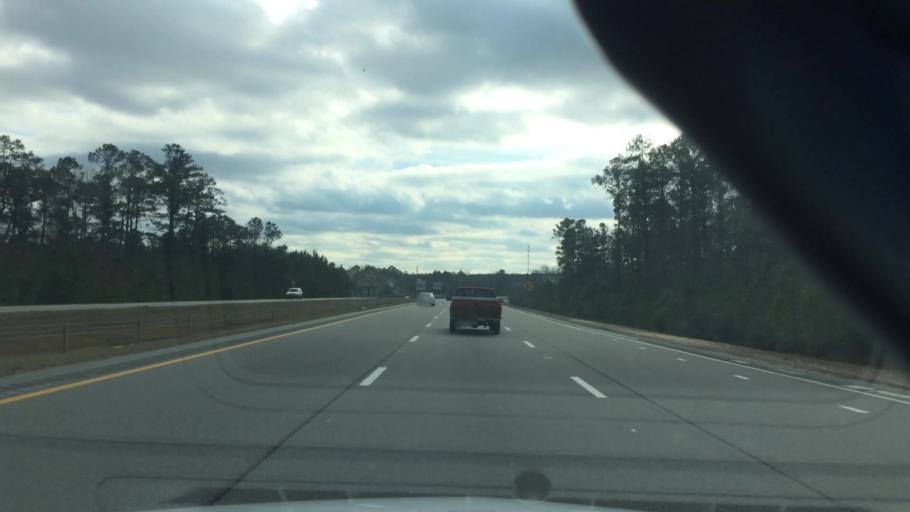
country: US
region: North Carolina
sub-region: Brunswick County
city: Leland
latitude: 34.1869
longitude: -78.0821
